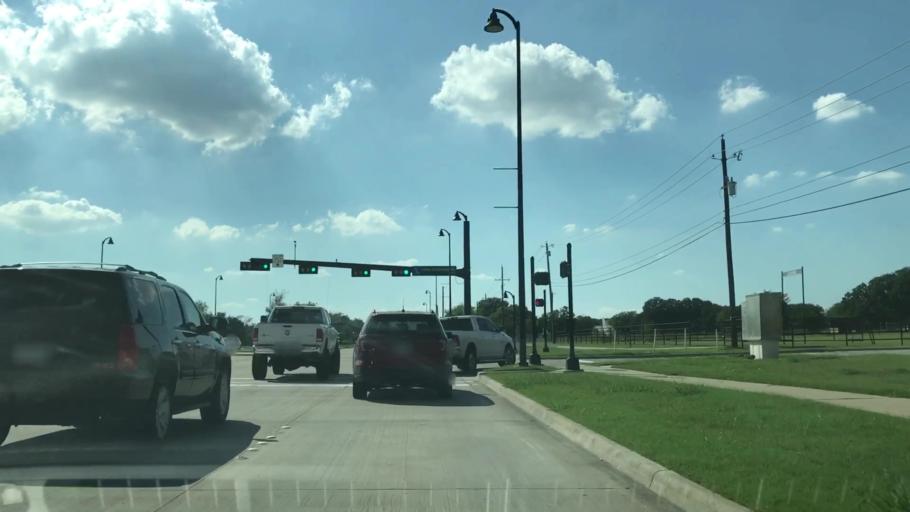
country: US
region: Texas
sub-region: Tarrant County
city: Keller
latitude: 32.9002
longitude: -97.2198
